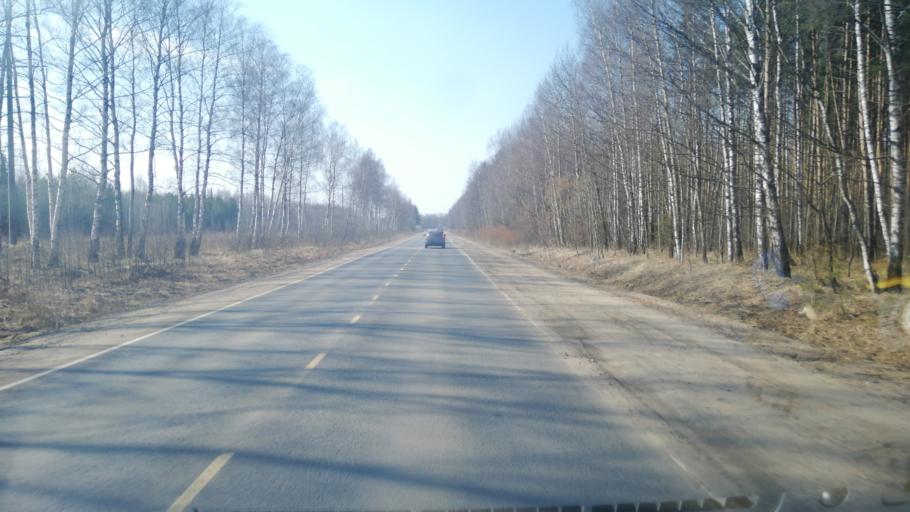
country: RU
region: Jaroslavl
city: Rostov
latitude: 57.2349
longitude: 39.4853
